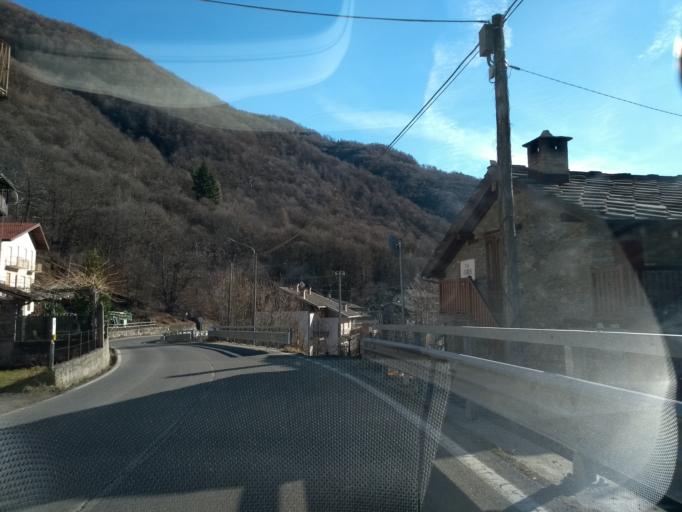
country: IT
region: Piedmont
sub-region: Provincia di Torino
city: Ceres
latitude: 45.3273
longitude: 7.3960
